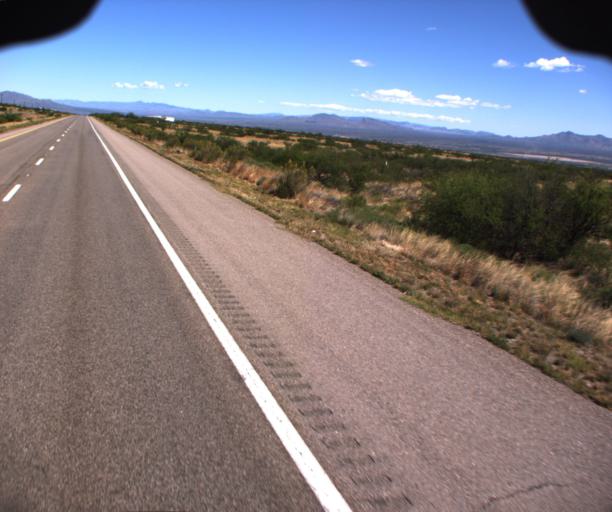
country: US
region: Arizona
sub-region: Cochise County
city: Whetstone
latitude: 31.9033
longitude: -110.3410
